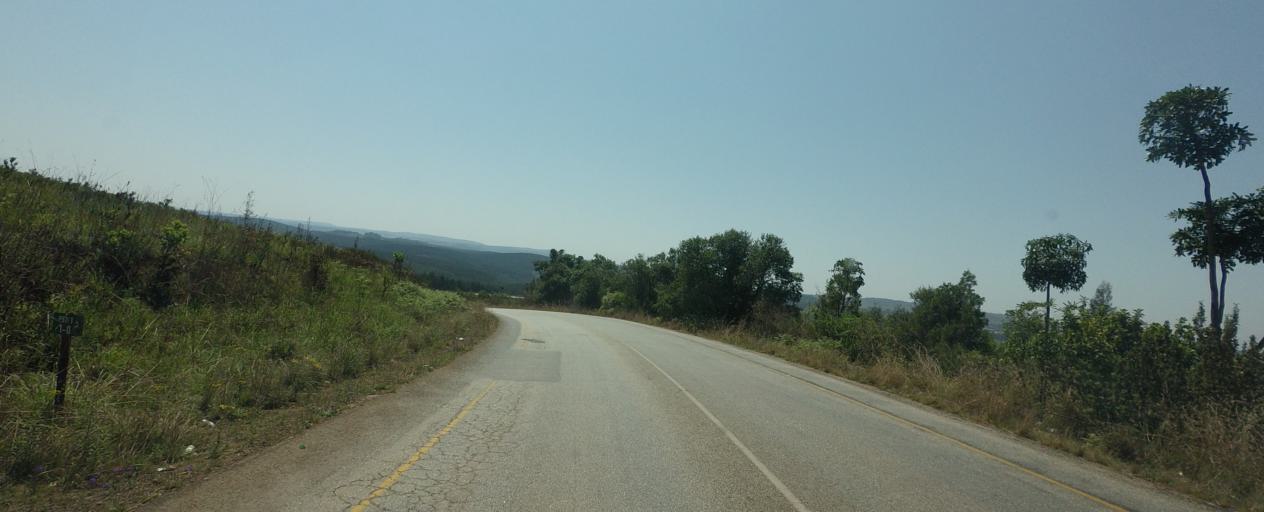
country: ZA
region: Mpumalanga
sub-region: Ehlanzeni District
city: Graksop
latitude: -24.9247
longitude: 30.8138
